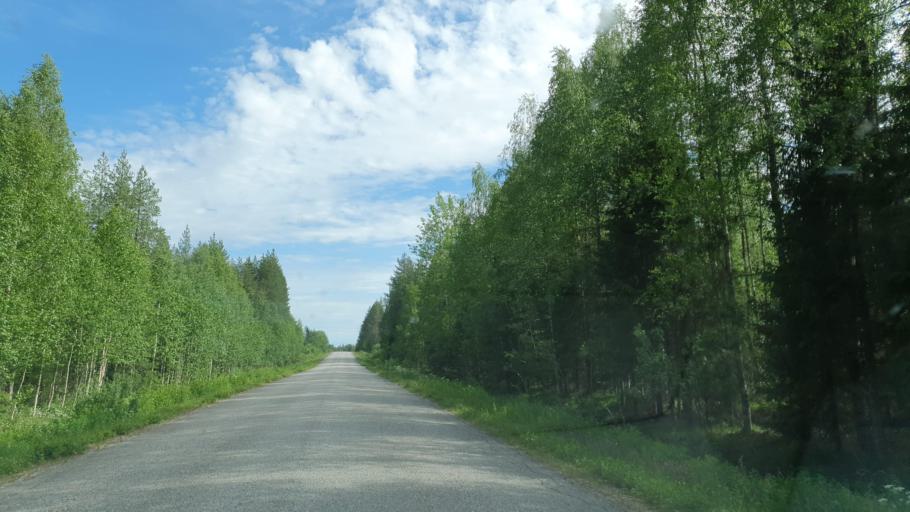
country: FI
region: Kainuu
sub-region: Kehys-Kainuu
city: Suomussalmi
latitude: 64.5902
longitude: 29.1066
